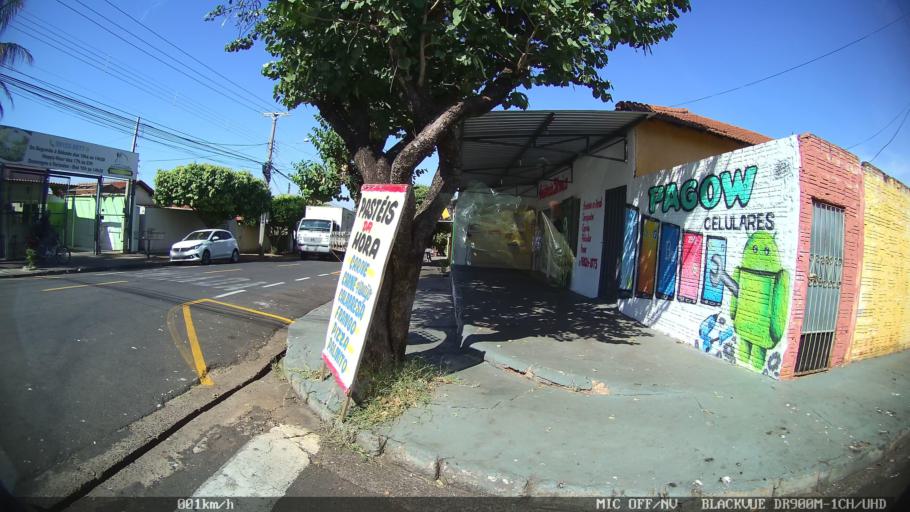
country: BR
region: Sao Paulo
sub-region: Sao Jose Do Rio Preto
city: Sao Jose do Rio Preto
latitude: -20.7696
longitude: -49.4085
